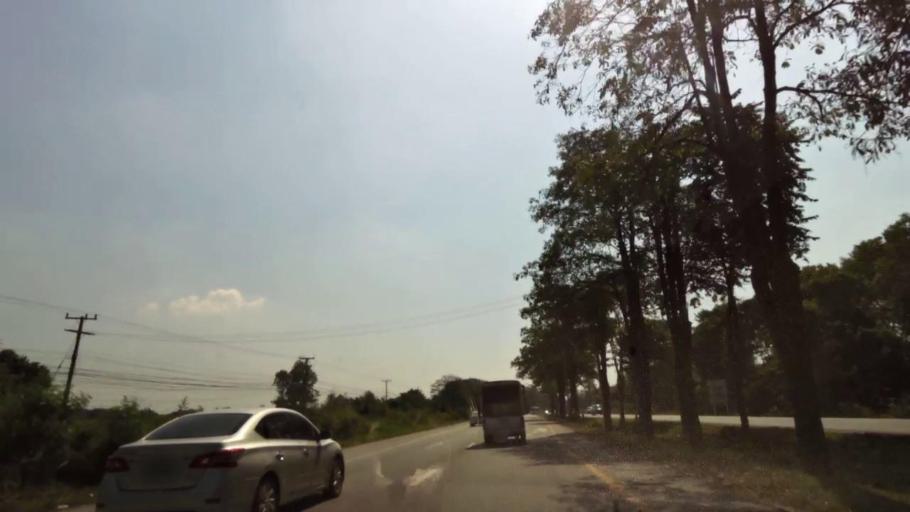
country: TH
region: Phichit
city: Bueng Na Rang
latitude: 16.1166
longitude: 100.1257
